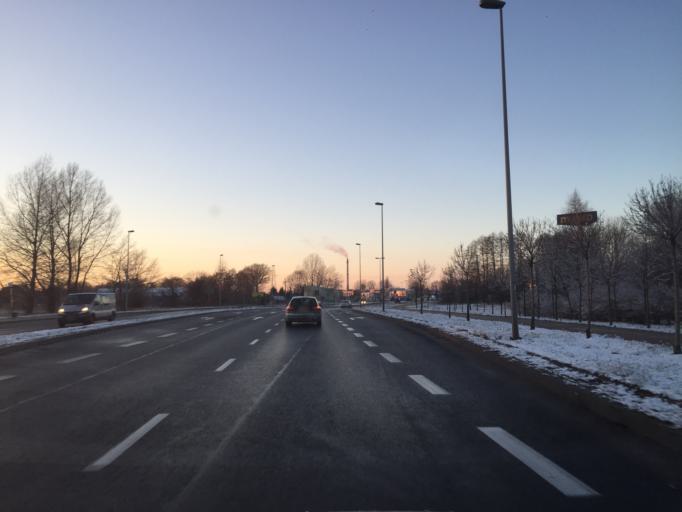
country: PL
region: Kujawsko-Pomorskie
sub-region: Powiat torunski
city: Lubicz Dolny
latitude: 53.0358
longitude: 18.6875
